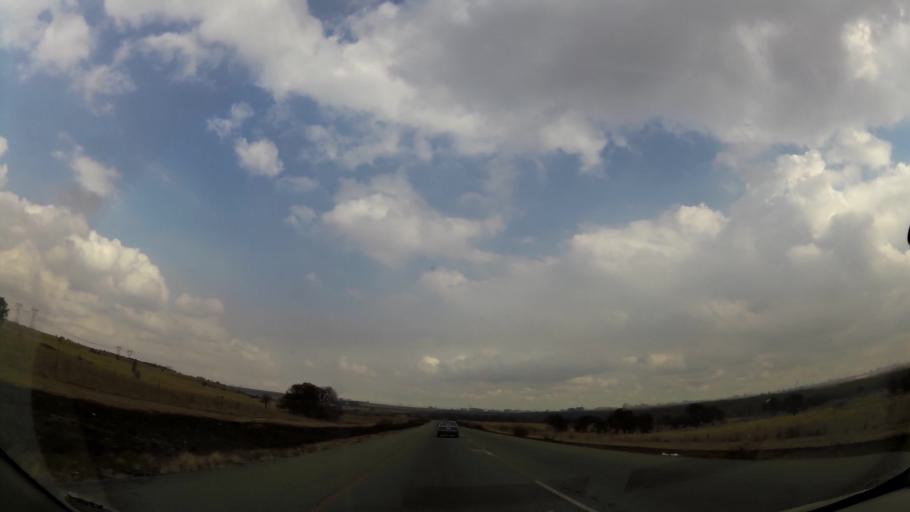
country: ZA
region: Orange Free State
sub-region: Fezile Dabi District Municipality
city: Sasolburg
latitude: -26.7975
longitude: 27.9150
